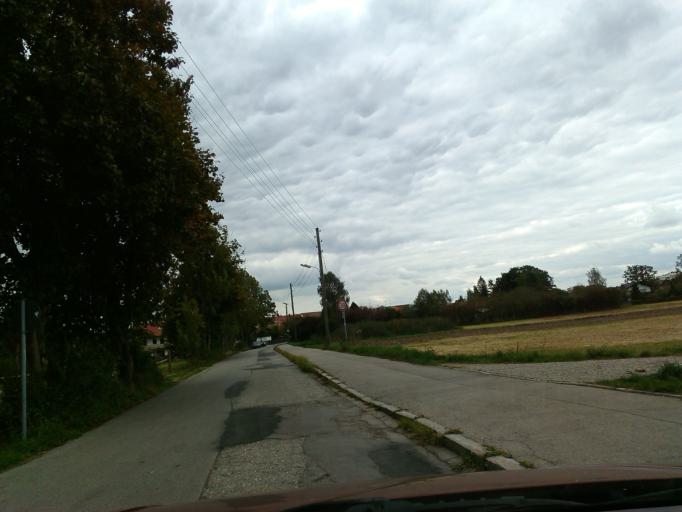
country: DE
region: Bavaria
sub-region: Upper Bavaria
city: Gauting
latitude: 48.0629
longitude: 11.3809
